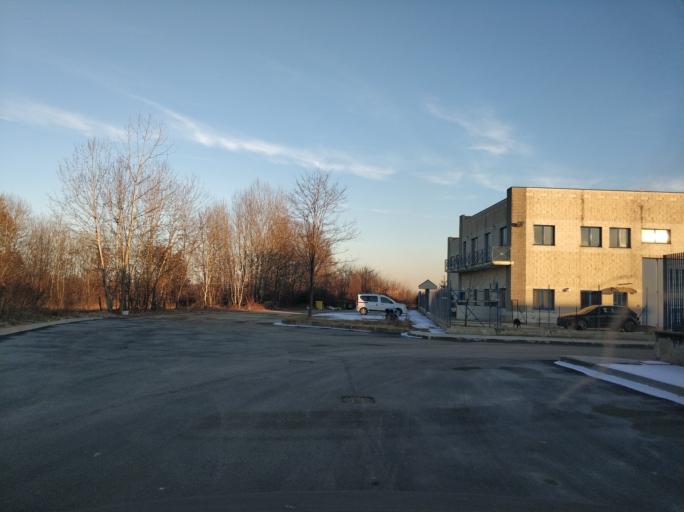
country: IT
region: Piedmont
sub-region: Provincia di Torino
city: Grosso
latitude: 45.2628
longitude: 7.5713
